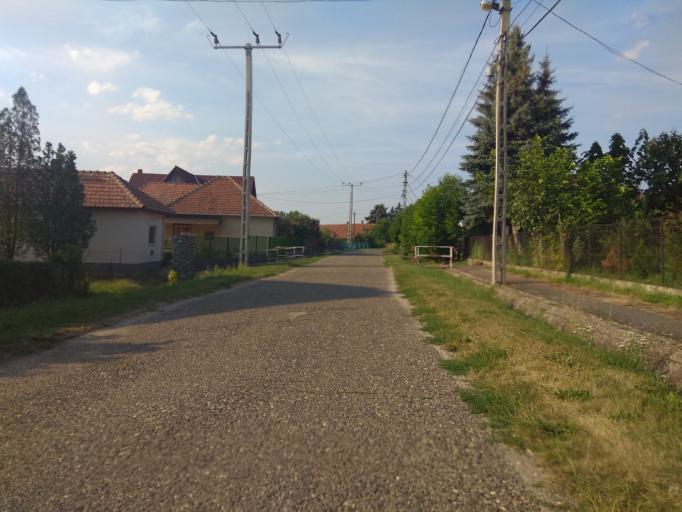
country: HU
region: Borsod-Abauj-Zemplen
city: Harsany
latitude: 47.9230
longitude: 20.7388
